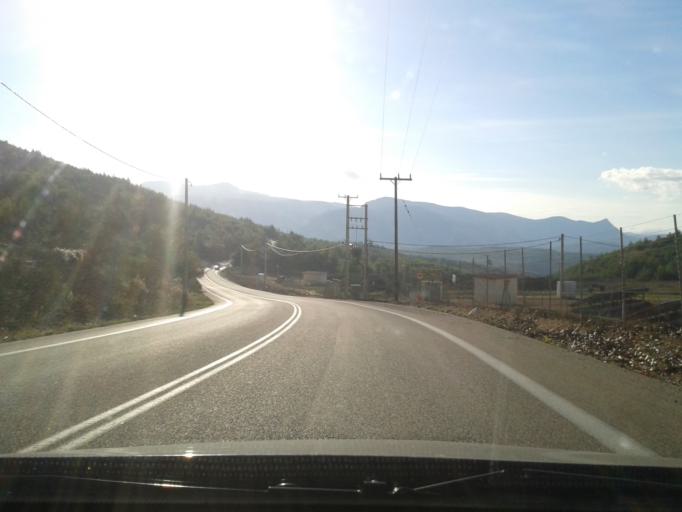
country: GR
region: Attica
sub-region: Nomarchia Anatolikis Attikis
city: Markopoulo Oropou
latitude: 38.2656
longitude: 23.8339
